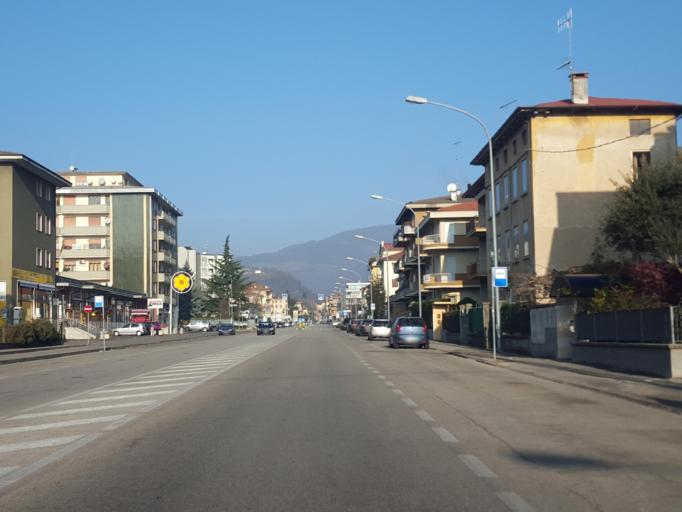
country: IT
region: Veneto
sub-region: Provincia di Vicenza
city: Valdagno
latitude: 45.6378
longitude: 11.3057
